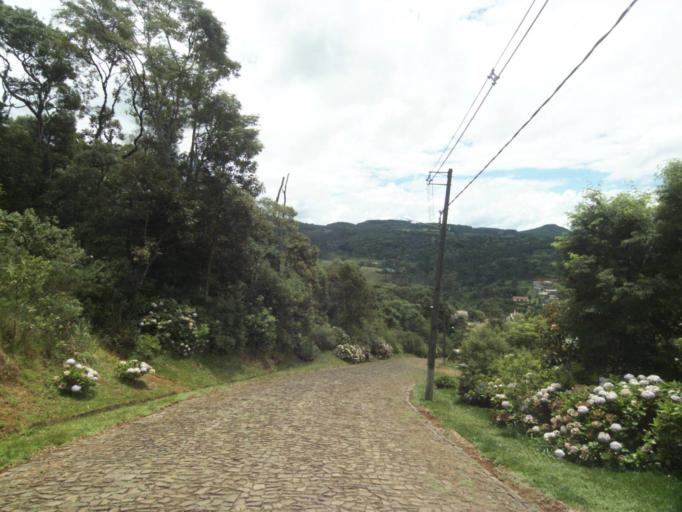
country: BR
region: Parana
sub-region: Pinhao
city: Pinhao
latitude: -26.1610
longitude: -51.5579
